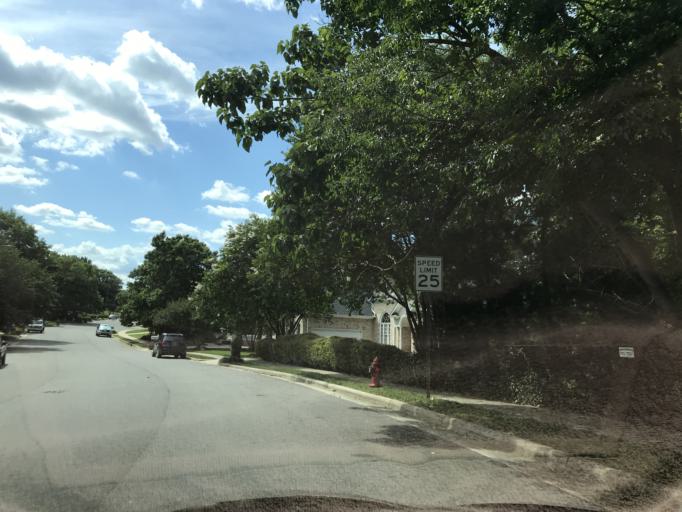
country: US
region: North Carolina
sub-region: Wake County
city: West Raleigh
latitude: 35.8830
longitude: -78.6846
